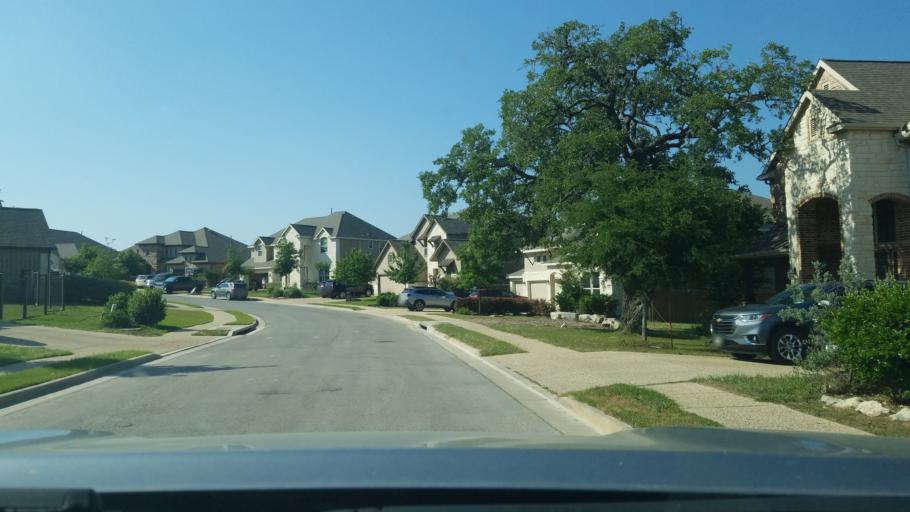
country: US
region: Texas
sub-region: Comal County
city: Bulverde
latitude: 29.7732
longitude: -98.4200
